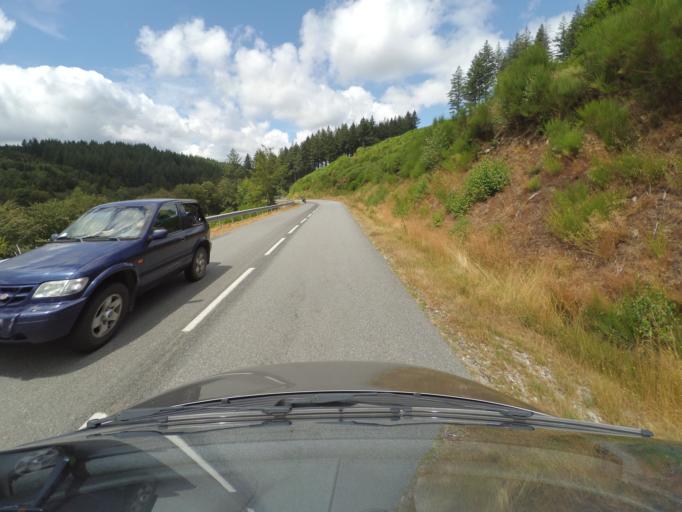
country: FR
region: Limousin
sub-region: Departement de la Creuse
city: Bourganeuf
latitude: 45.9137
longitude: 1.8538
